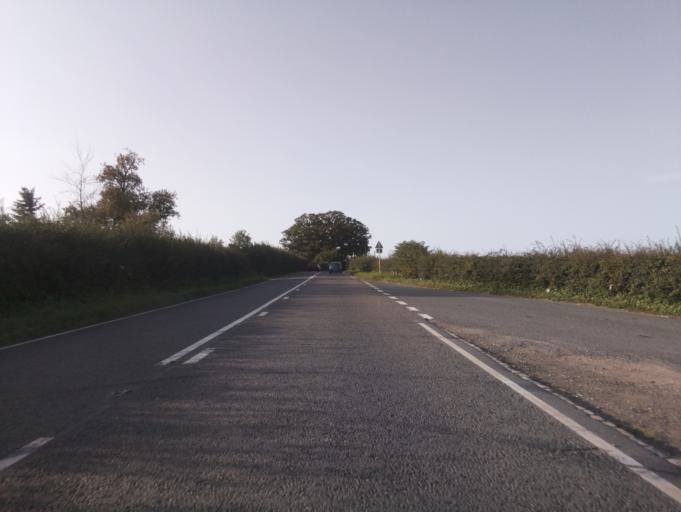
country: GB
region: England
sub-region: Gloucestershire
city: Gloucester
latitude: 51.8999
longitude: -2.2874
